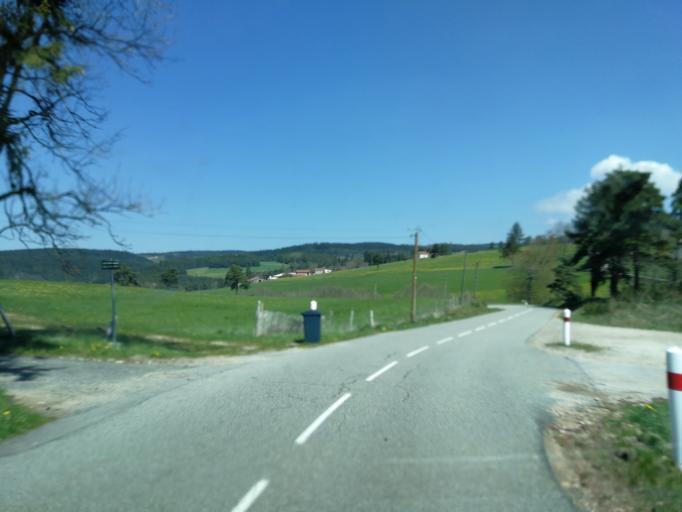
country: FR
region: Rhone-Alpes
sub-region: Departement de la Loire
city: Marlhes
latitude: 45.2922
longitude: 4.3876
